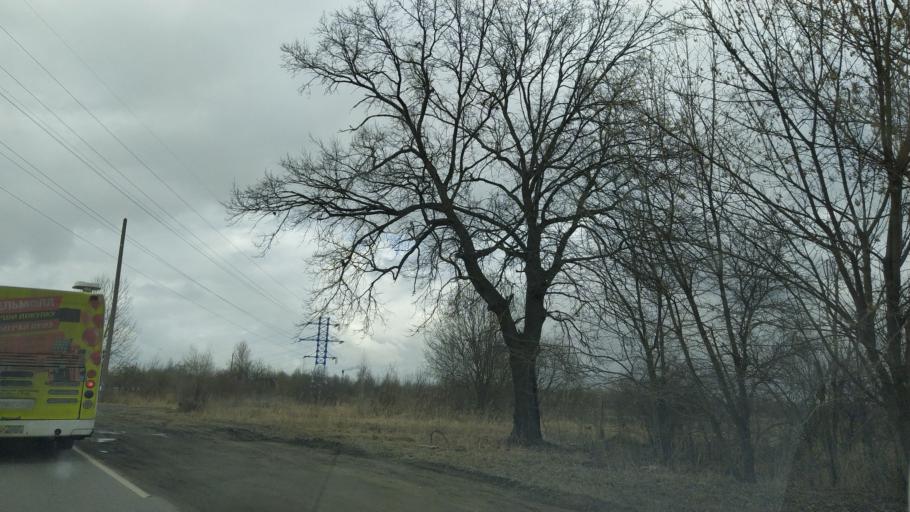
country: RU
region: St.-Petersburg
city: Tyarlevo
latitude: 59.7139
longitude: 30.4368
